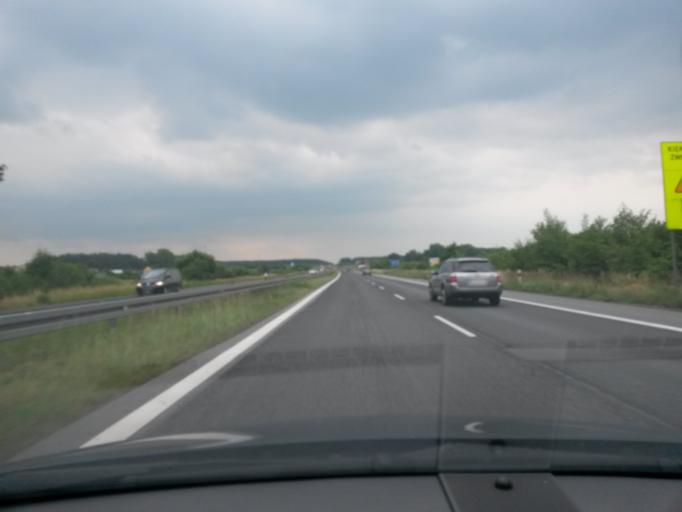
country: PL
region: Silesian Voivodeship
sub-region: Powiat czestochowski
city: Borowno
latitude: 51.0009
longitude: 19.2940
